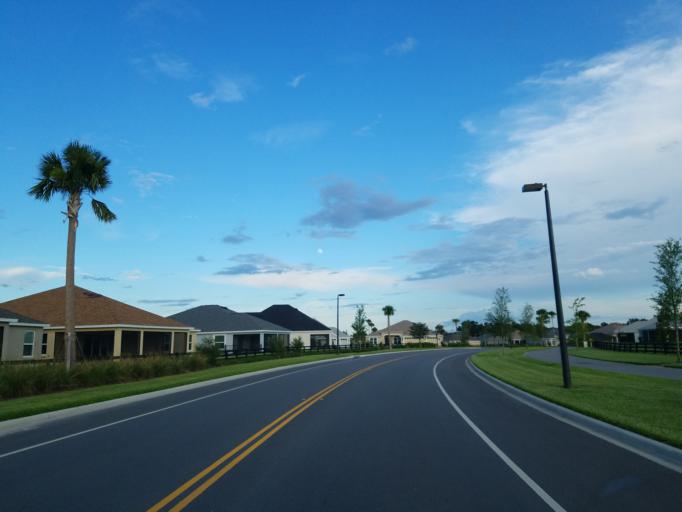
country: US
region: Florida
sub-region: Sumter County
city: Wildwood
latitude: 28.7938
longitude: -82.0257
